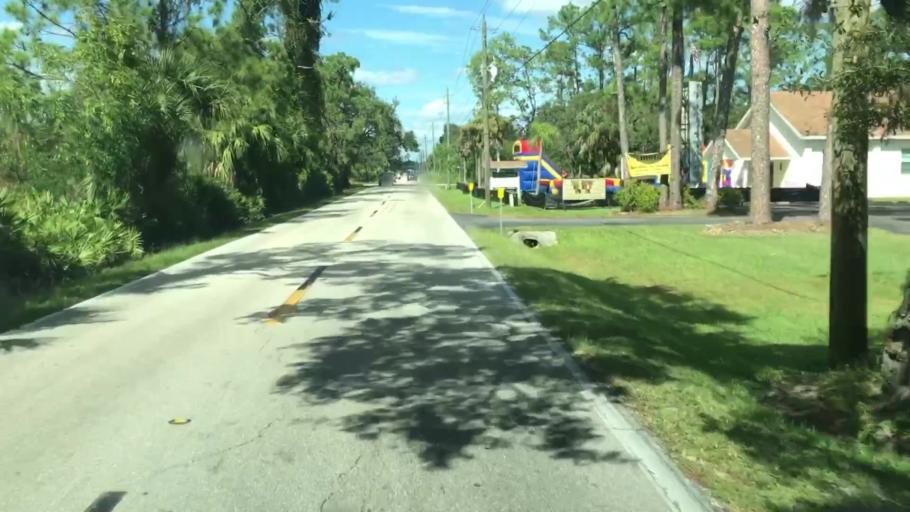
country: US
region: Florida
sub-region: Lee County
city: Alva
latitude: 26.7006
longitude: -81.6009
